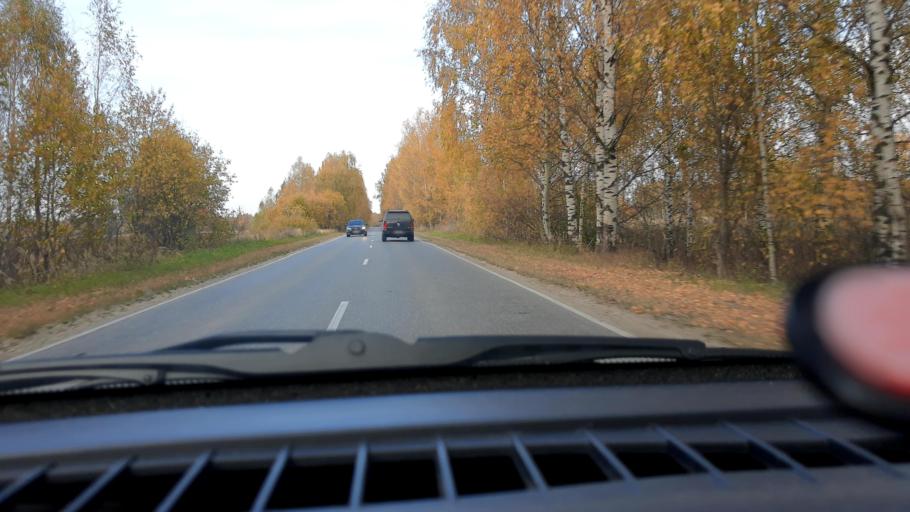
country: RU
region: Nizjnij Novgorod
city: Neklyudovo
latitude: 56.5208
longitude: 43.8362
